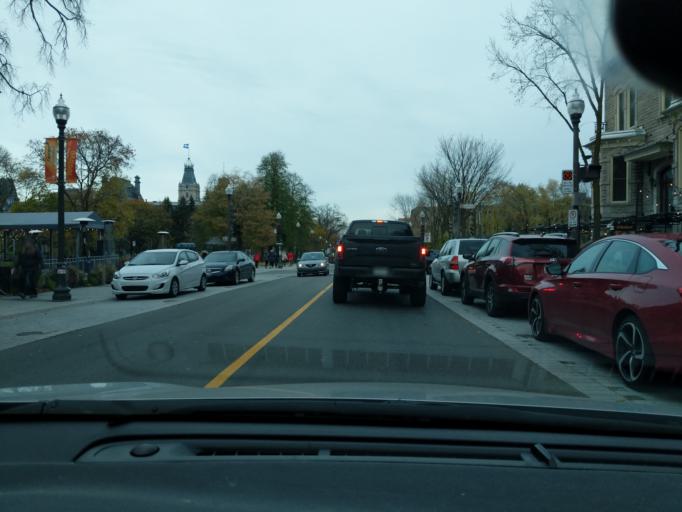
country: CA
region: Quebec
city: Quebec
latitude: 46.8067
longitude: -71.2157
